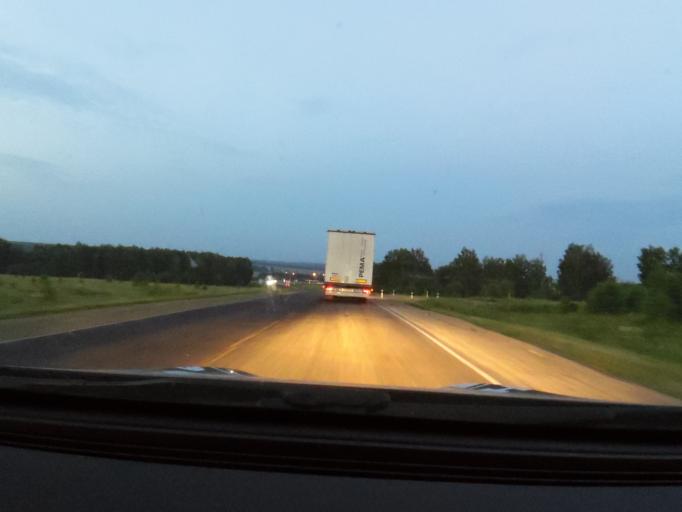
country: RU
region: Bashkortostan
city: Duvan
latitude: 56.0707
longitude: 58.1708
